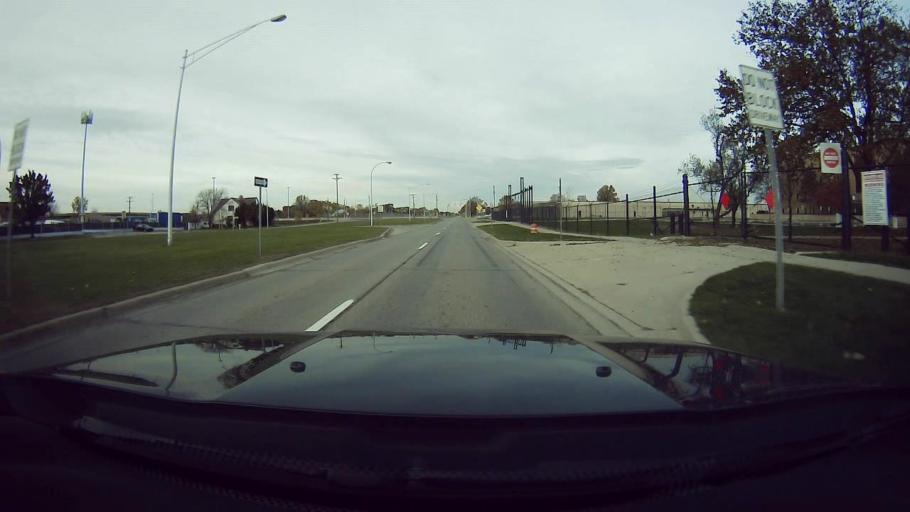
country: US
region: Michigan
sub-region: Macomb County
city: Center Line
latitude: 42.4917
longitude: -83.0426
